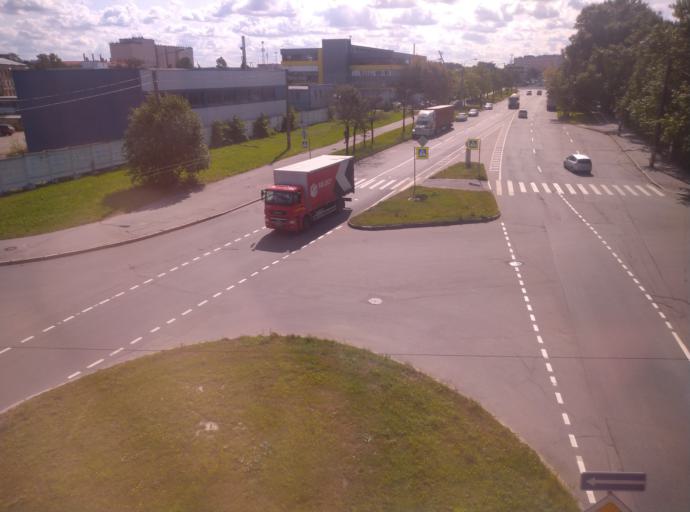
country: RU
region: St.-Petersburg
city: Centralniy
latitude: 59.9118
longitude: 30.3974
